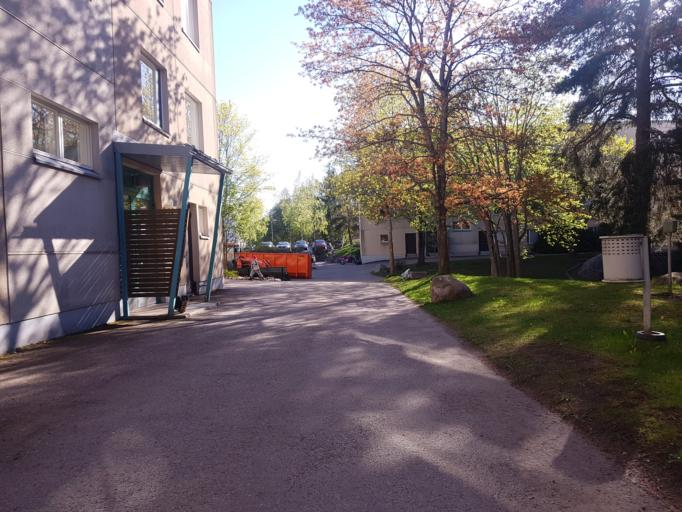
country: FI
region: Uusimaa
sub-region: Helsinki
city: Vantaa
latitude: 60.2343
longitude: 24.9985
